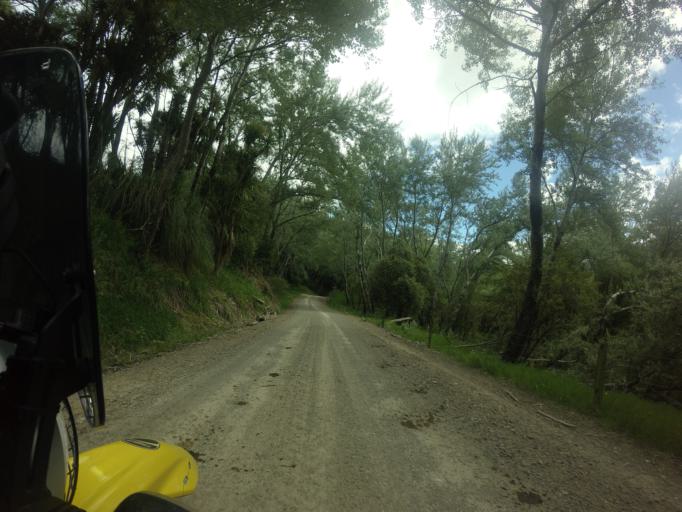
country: NZ
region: Hawke's Bay
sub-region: Wairoa District
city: Wairoa
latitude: -39.0052
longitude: 177.7616
